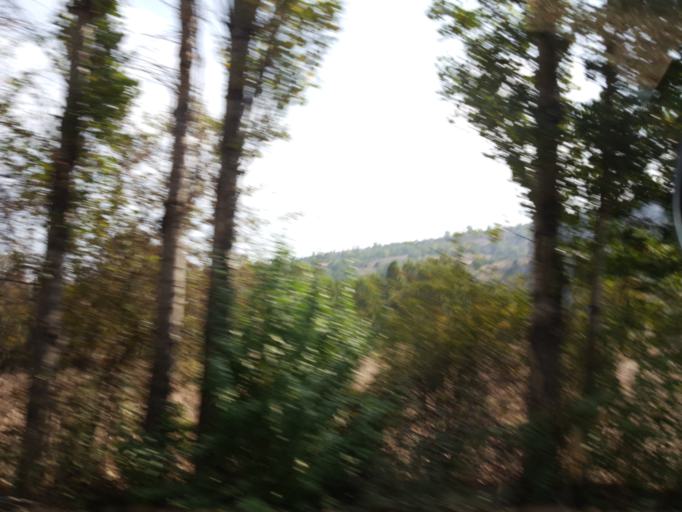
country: TR
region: Tokat
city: Zile
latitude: 40.3634
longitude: 35.8526
